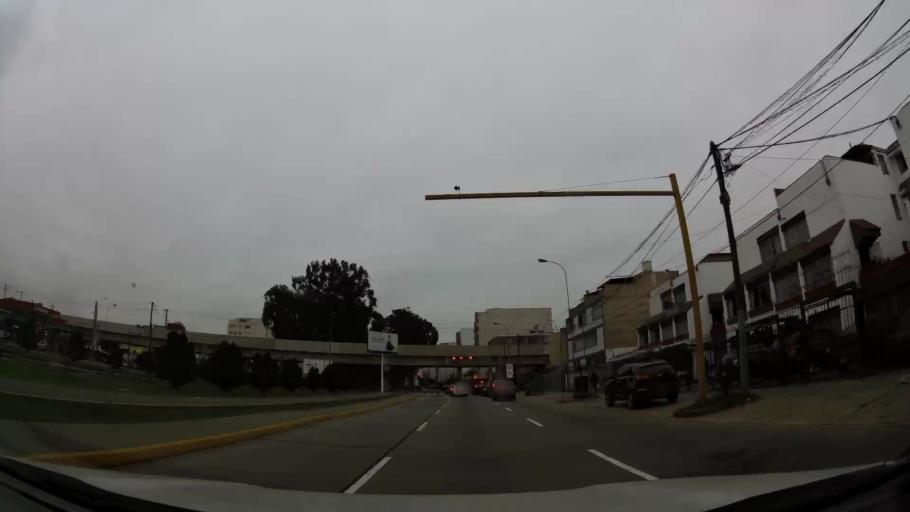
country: PE
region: Lima
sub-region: Lima
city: San Luis
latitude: -12.0945
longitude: -77.0034
